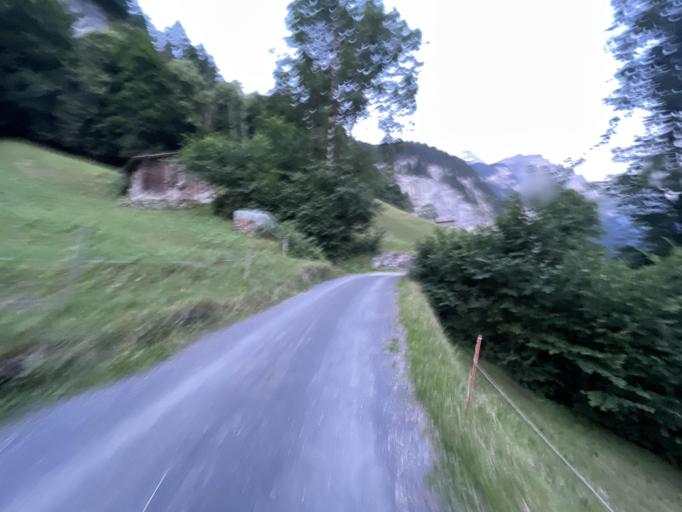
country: CH
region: Bern
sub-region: Interlaken-Oberhasli District
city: Lauterbrunnen
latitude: 46.5998
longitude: 7.9123
